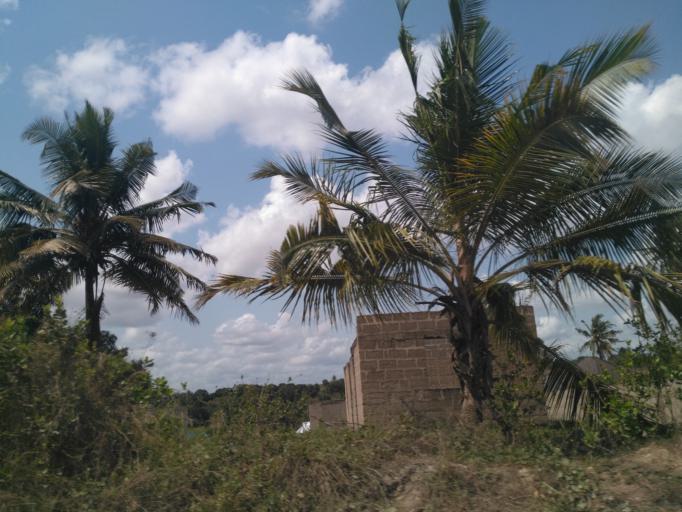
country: TZ
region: Dar es Salaam
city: Dar es Salaam
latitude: -6.8811
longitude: 39.3312
